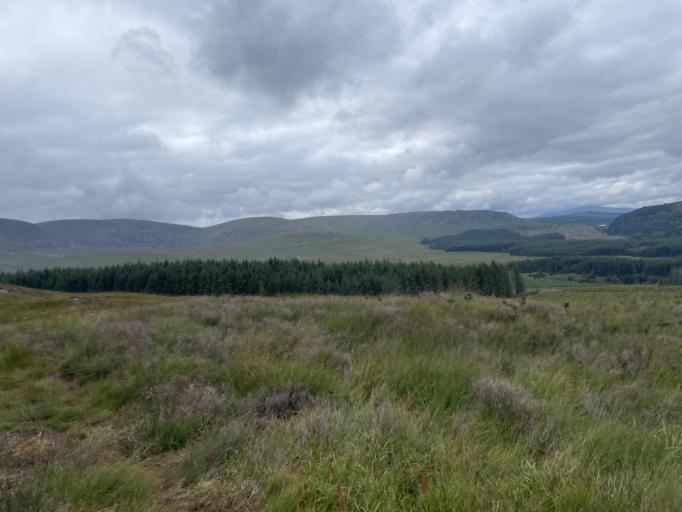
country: GB
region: Scotland
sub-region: Dumfries and Galloway
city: Newton Stewart
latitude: 54.9516
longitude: -4.2706
